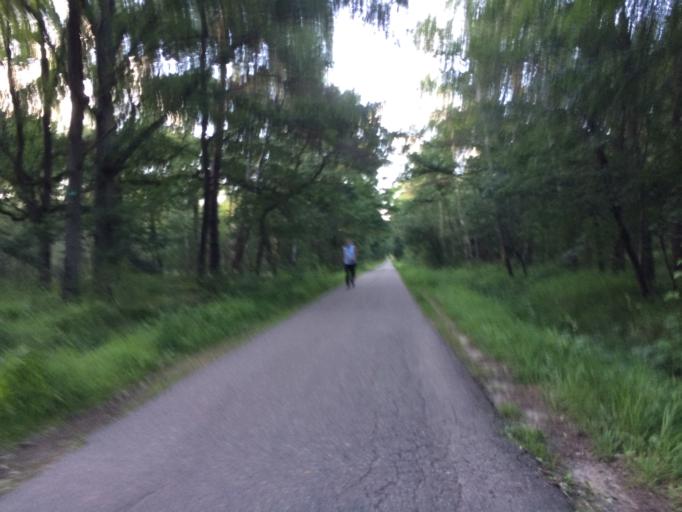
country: FR
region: Ile-de-France
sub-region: Departement de l'Essonne
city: Soisy-sur-Seine
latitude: 48.6728
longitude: 2.4627
